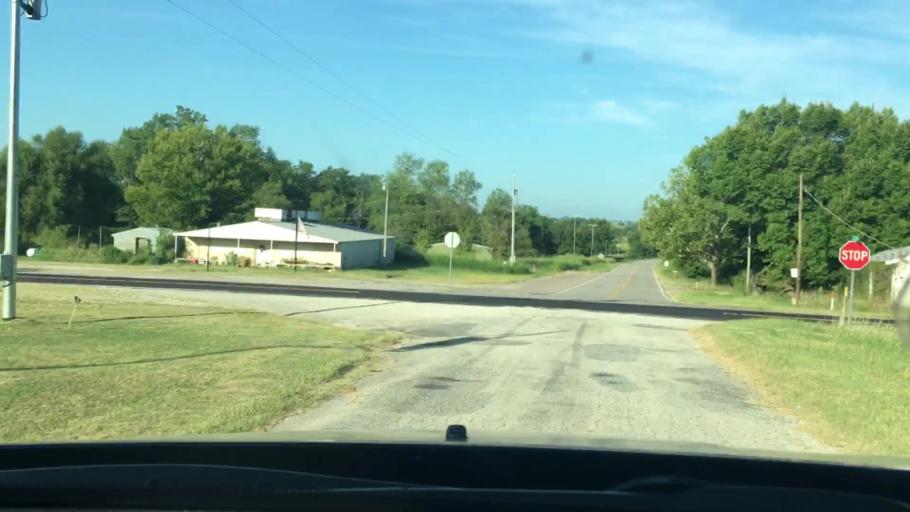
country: US
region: Oklahoma
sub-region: Pontotoc County
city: Ada
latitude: 34.7008
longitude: -96.4317
